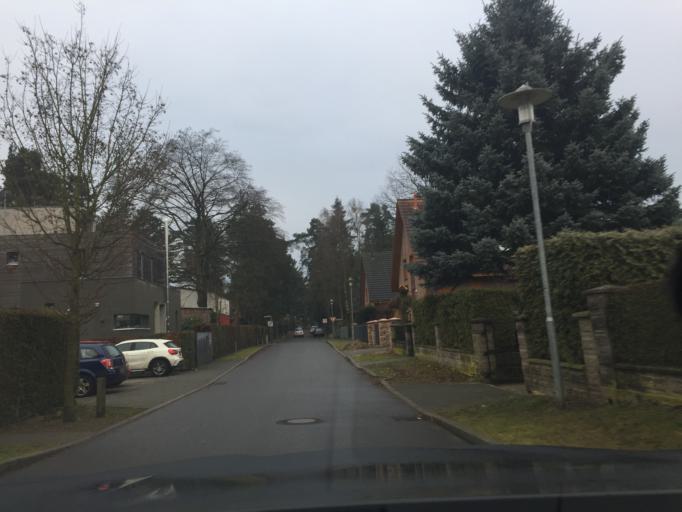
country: DE
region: Berlin
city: Kladow
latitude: 52.4620
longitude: 13.1030
